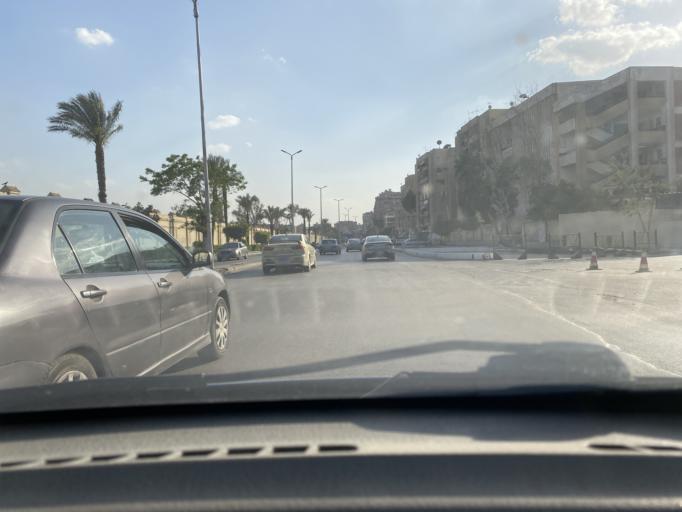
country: EG
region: Muhafazat al Qahirah
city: Cairo
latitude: 30.0940
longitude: 31.2952
